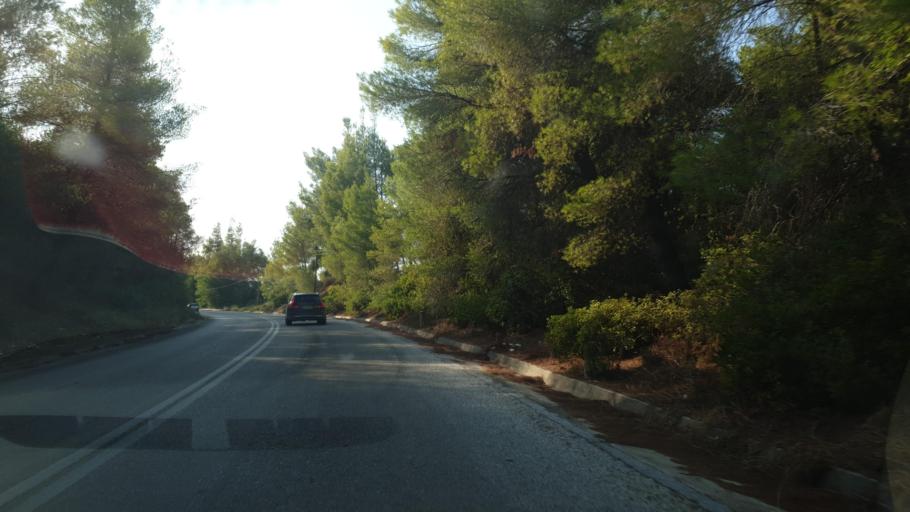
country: GR
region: Central Macedonia
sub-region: Nomos Chalkidikis
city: Neos Marmaras
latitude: 40.1792
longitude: 23.8272
